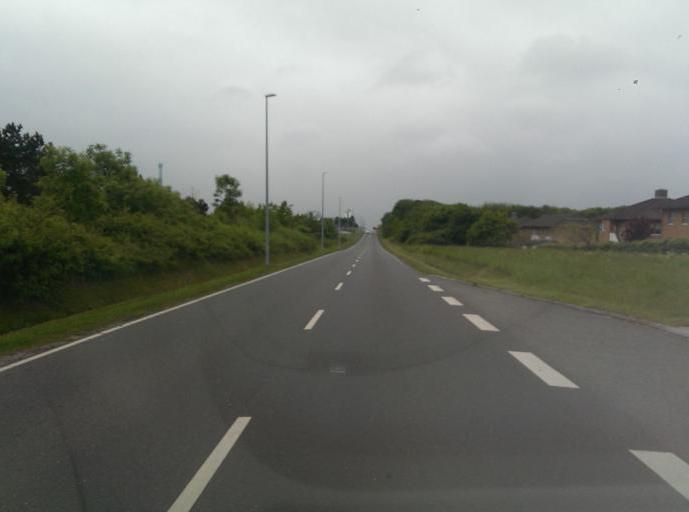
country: DK
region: South Denmark
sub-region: Fano Kommune
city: Nordby
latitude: 55.5301
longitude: 8.3593
